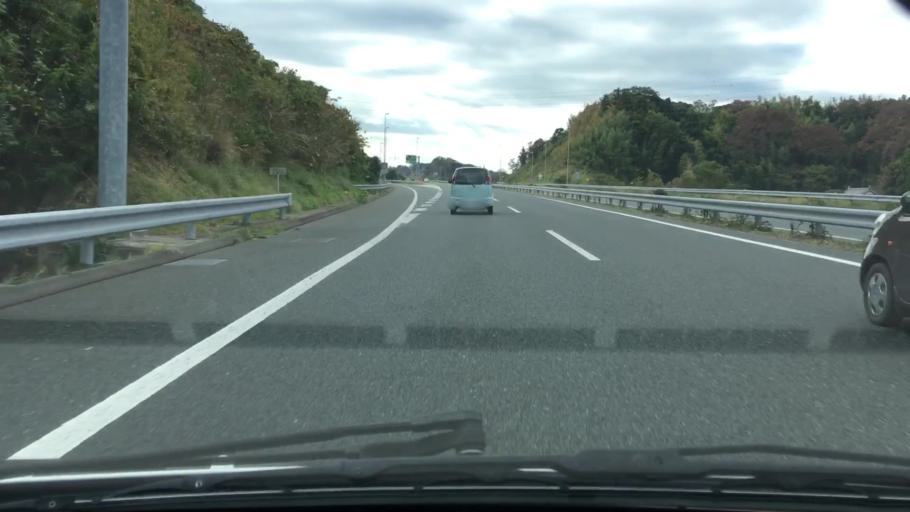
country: JP
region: Chiba
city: Kimitsu
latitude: 35.2556
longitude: 139.8937
